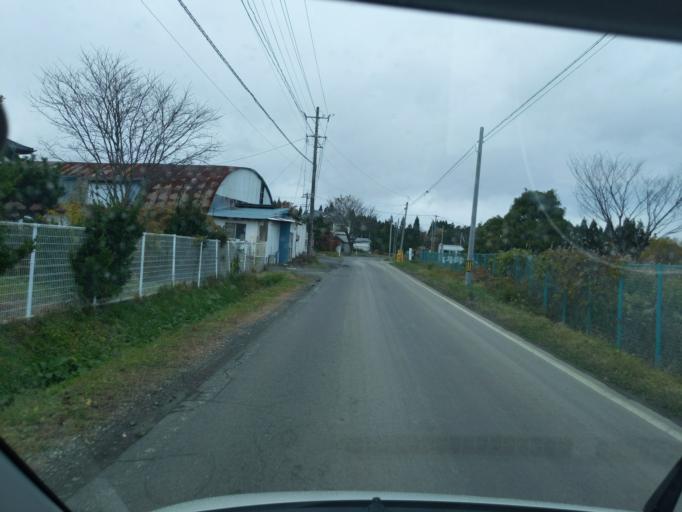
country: JP
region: Iwate
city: Mizusawa
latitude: 39.0525
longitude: 141.0654
